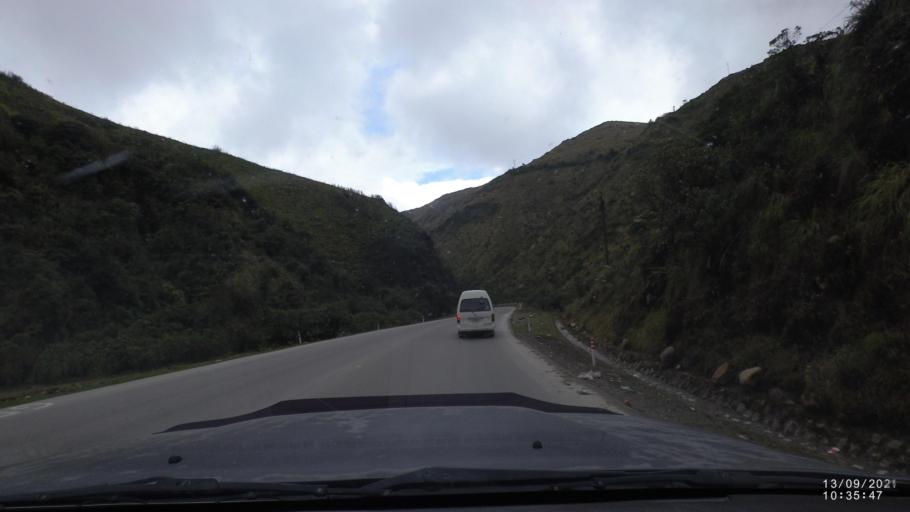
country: BO
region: Cochabamba
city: Colomi
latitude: -17.2154
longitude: -65.8912
